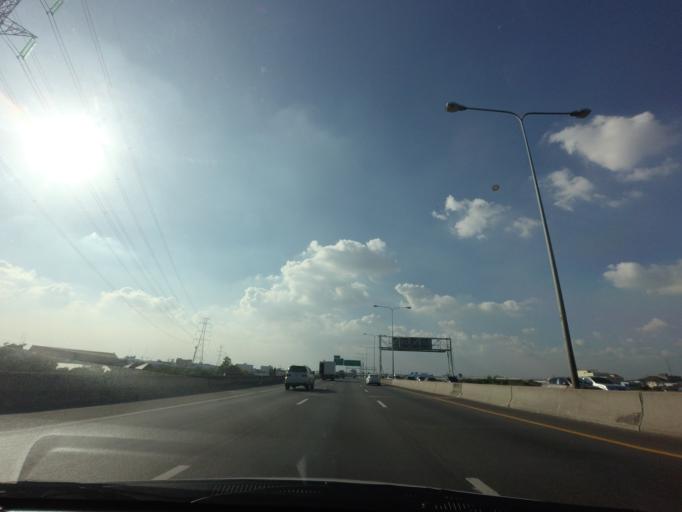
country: TH
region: Samut Prakan
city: Samut Prakan
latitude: 13.6237
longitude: 100.6011
